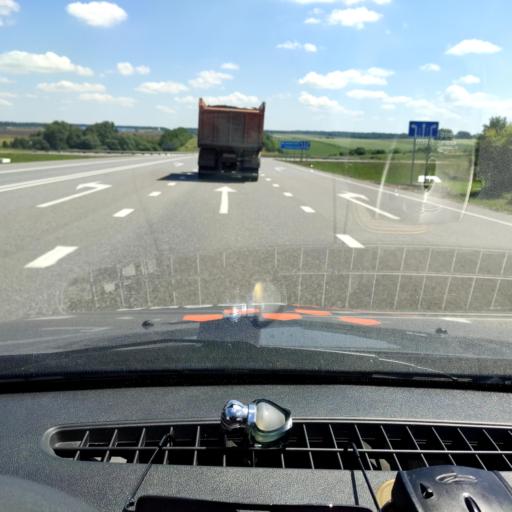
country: RU
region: Orjol
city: Zmiyevka
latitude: 52.8290
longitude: 36.2713
